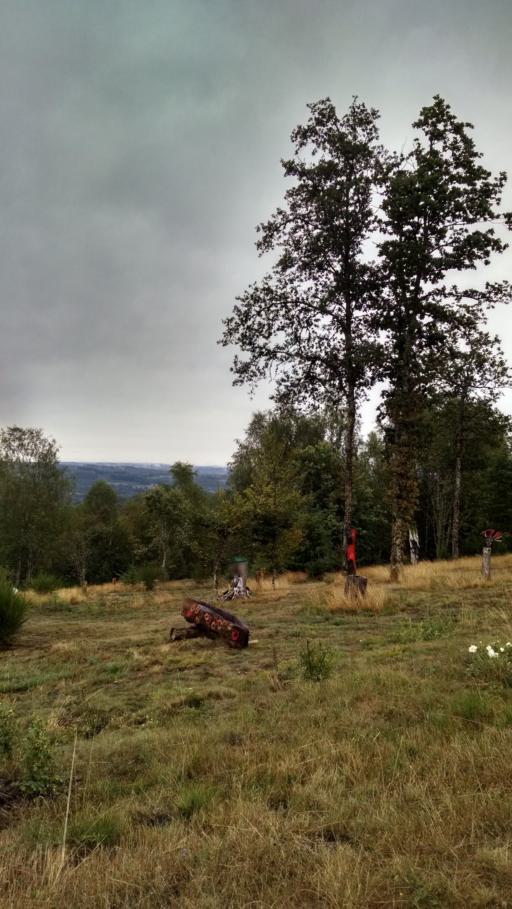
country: FR
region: Limousin
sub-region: Departement de la Creuse
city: La Courtine
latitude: 45.6914
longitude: 2.1252
